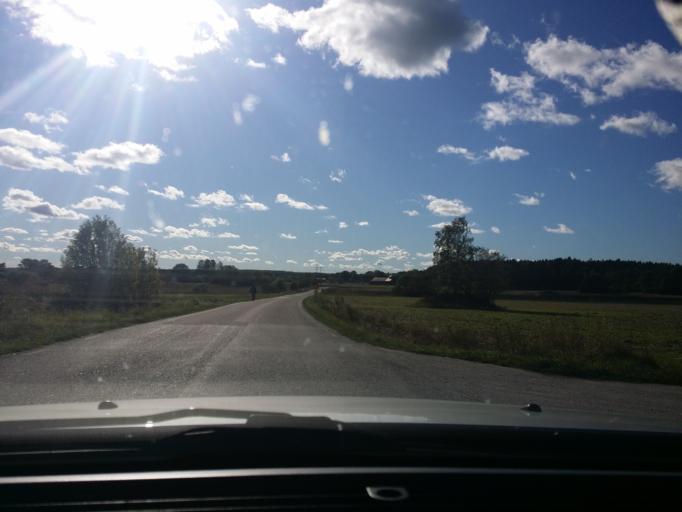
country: SE
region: Vaestmanland
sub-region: Vasteras
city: Vasteras
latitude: 59.5509
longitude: 16.4593
